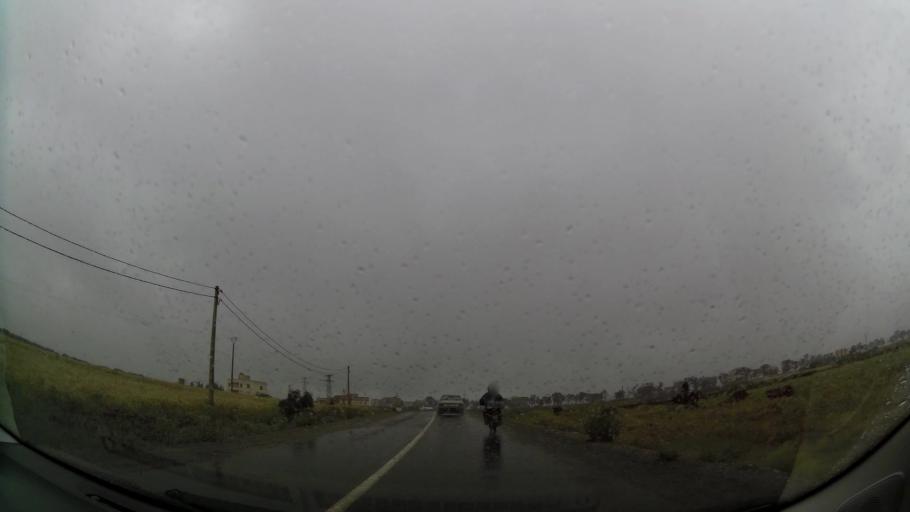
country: MA
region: Oriental
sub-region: Nador
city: Boudinar
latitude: 35.1338
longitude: -3.6251
